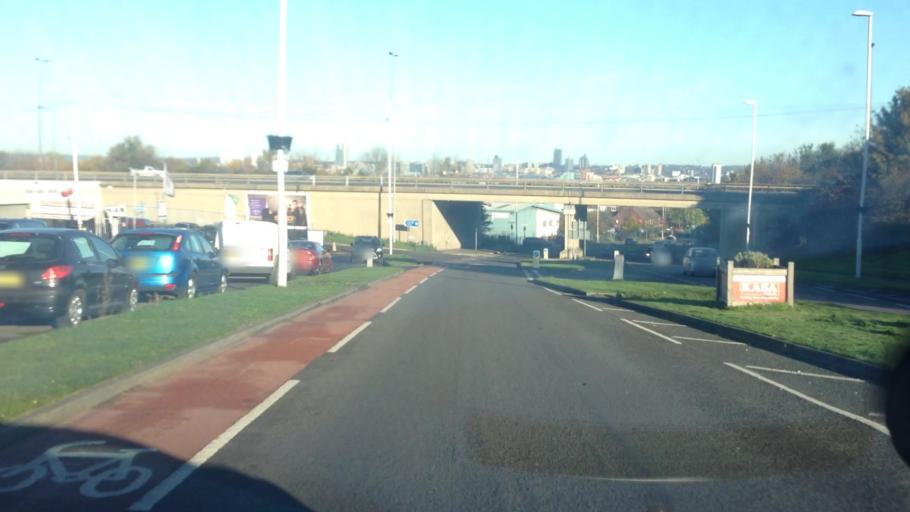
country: GB
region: England
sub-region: City and Borough of Leeds
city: Leeds
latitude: 53.7696
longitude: -1.5307
